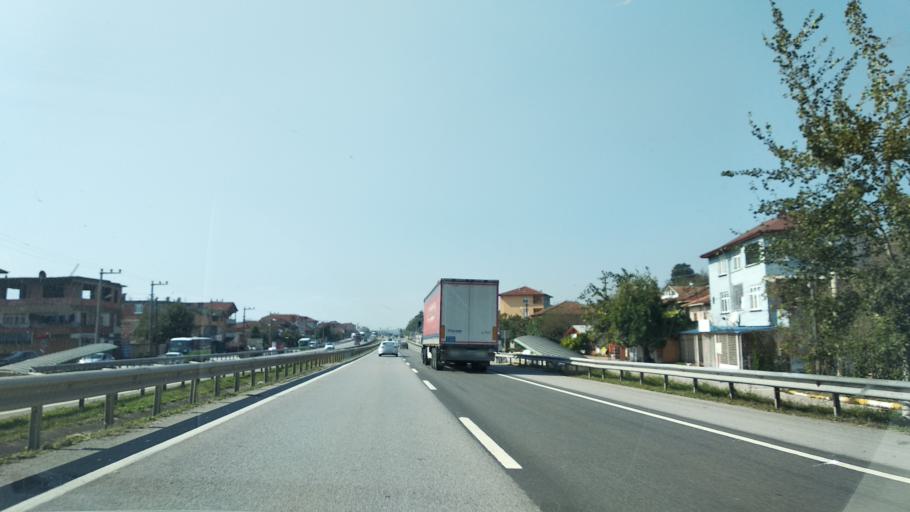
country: TR
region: Sakarya
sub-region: Merkez
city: Sapanca
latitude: 40.7344
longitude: 30.2269
